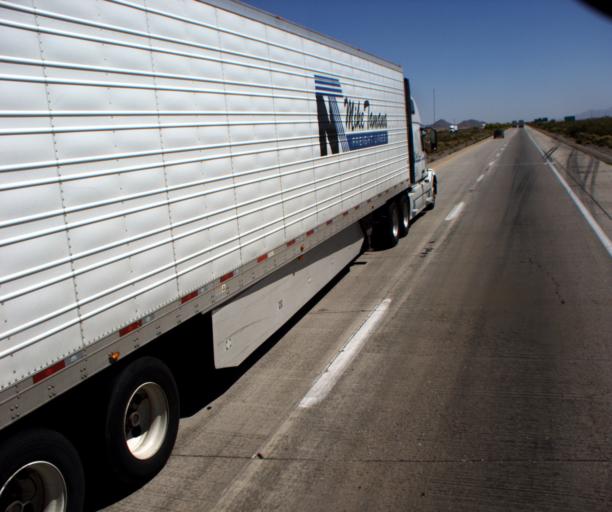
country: US
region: Arizona
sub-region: Maricopa County
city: Buckeye
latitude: 33.4453
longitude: -112.7050
